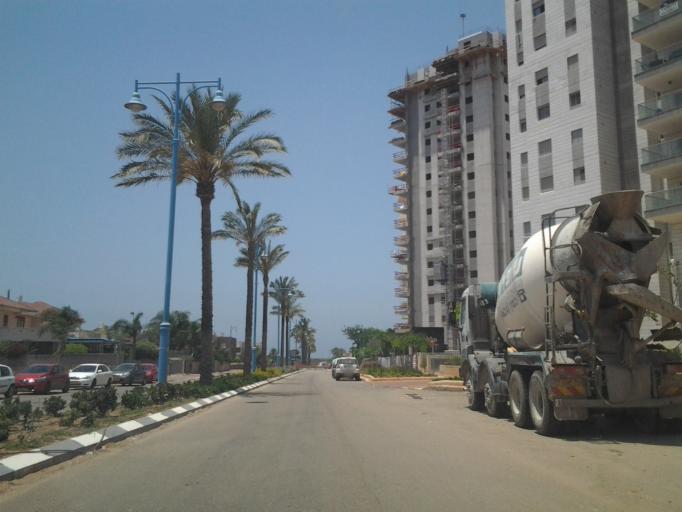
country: IL
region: Haifa
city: Hadera
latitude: 32.4289
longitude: 34.8851
